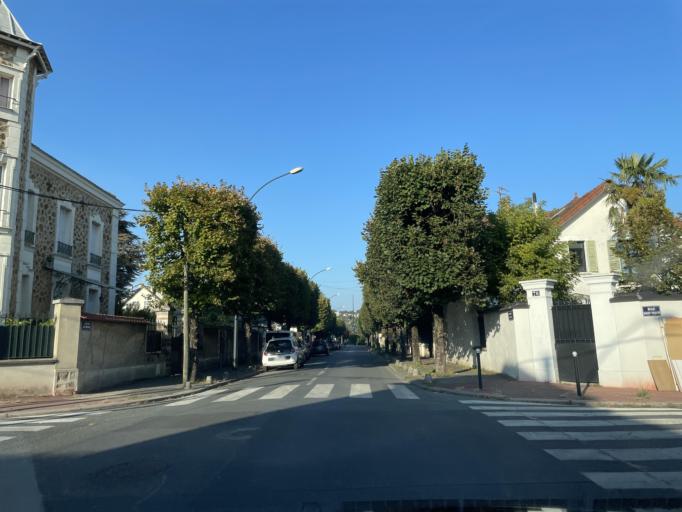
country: FR
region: Ile-de-France
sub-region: Departement du Val-de-Marne
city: Chennevieres-sur-Marne
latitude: 48.7994
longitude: 2.5178
